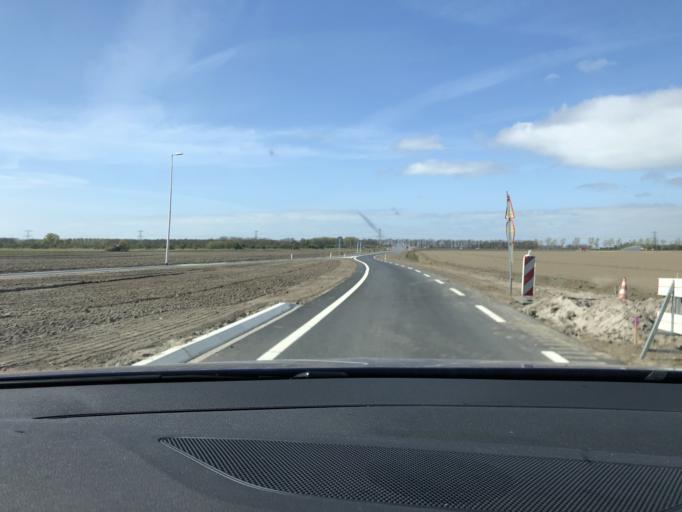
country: NL
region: Flevoland
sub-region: Gemeente Lelystad
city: Lelystad
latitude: 52.4581
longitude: 5.4837
